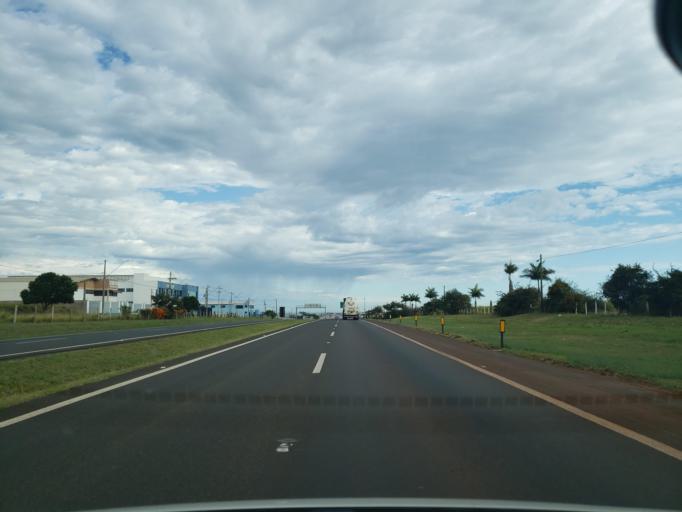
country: BR
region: Sao Paulo
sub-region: Jau
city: Jau
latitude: -22.2666
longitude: -48.5073
